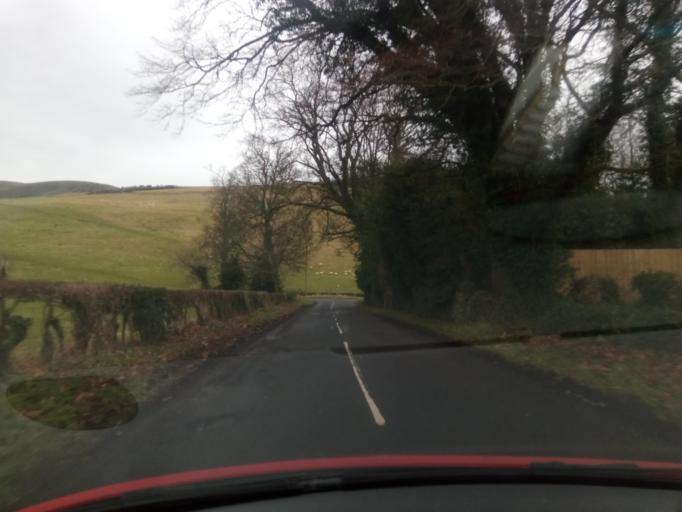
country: GB
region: England
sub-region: Northumberland
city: Kirknewton
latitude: 55.5664
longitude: -2.1358
